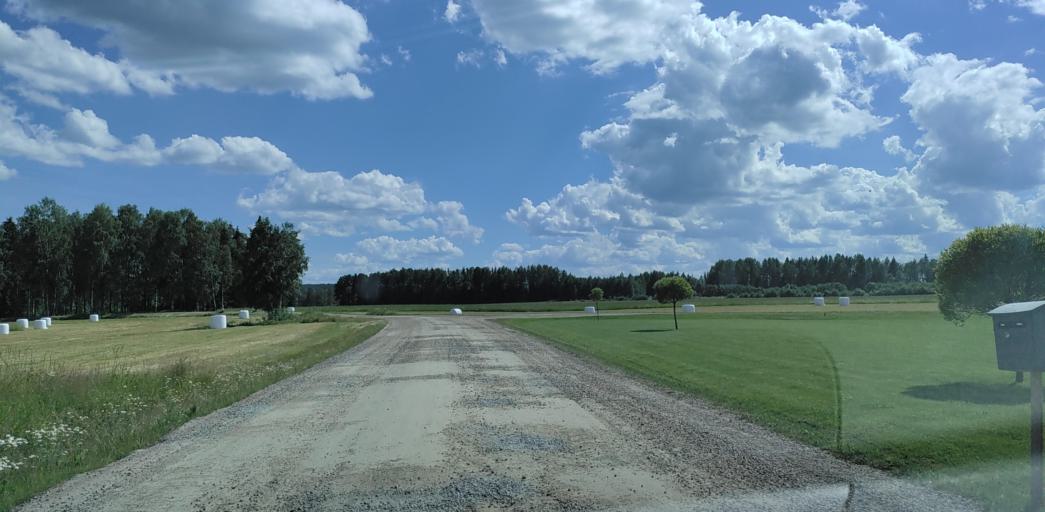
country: SE
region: Vaermland
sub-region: Hagfors Kommun
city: Ekshaerad
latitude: 60.1231
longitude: 13.4816
